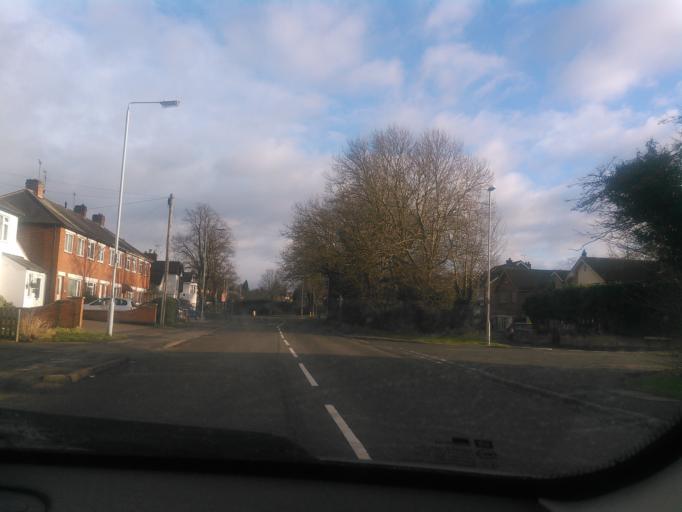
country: GB
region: England
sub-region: Leicestershire
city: Oadby
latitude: 52.5961
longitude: -1.0737
